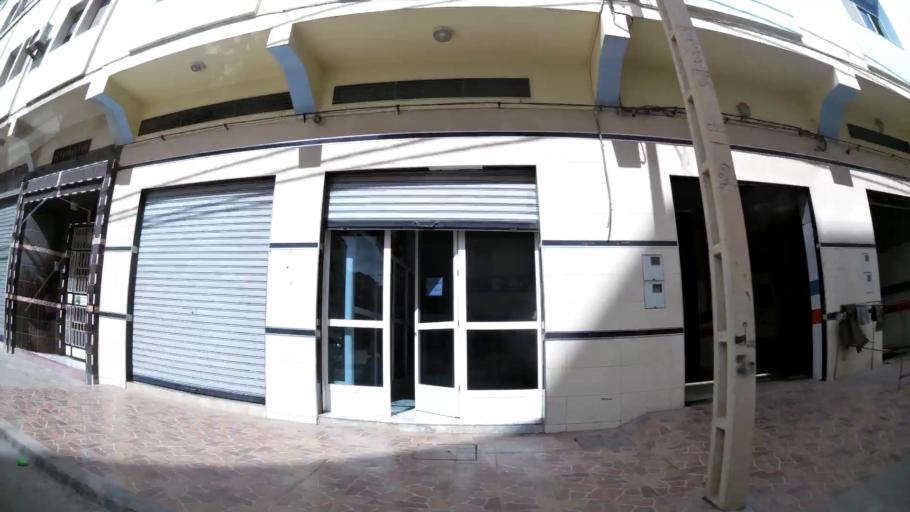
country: MA
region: Oriental
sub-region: Nador
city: Nador
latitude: 35.1620
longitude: -2.9285
